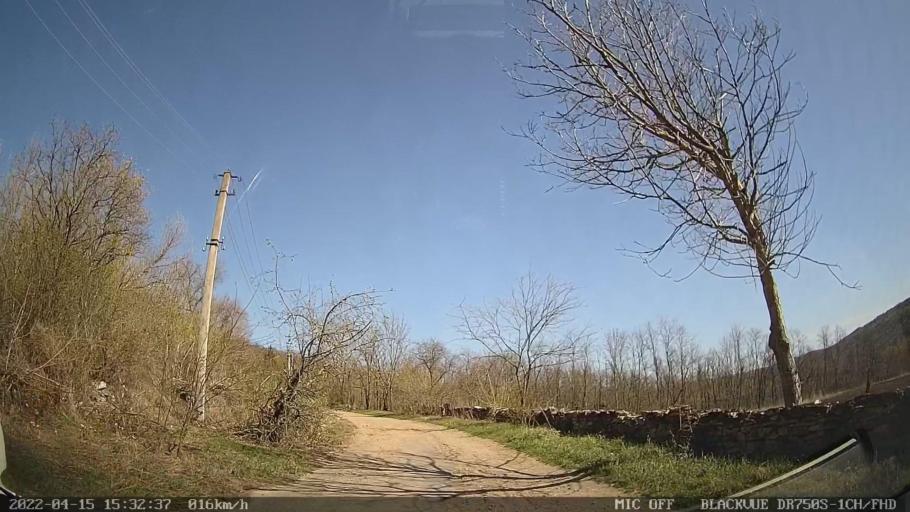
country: MD
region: Raionul Ocnita
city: Otaci
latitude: 48.3508
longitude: 27.9211
